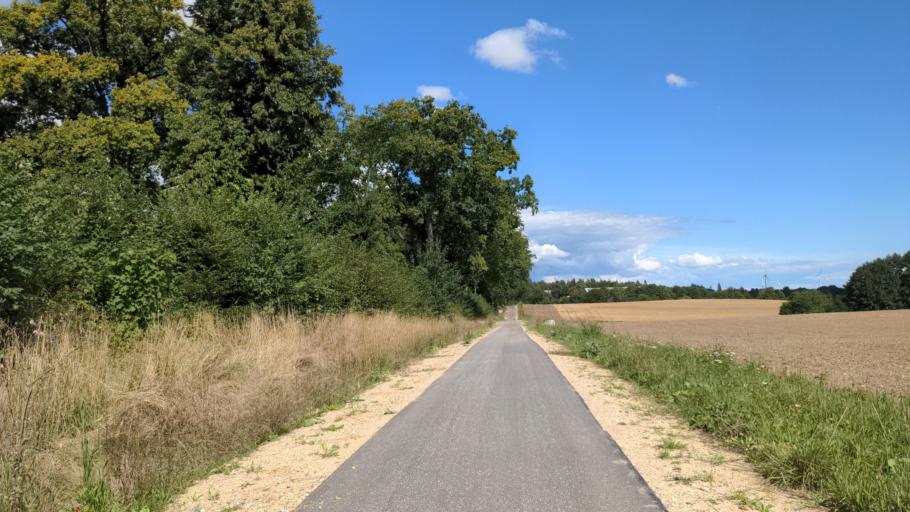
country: DE
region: Schleswig-Holstein
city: Beschendorf
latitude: 54.2066
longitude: 10.8580
